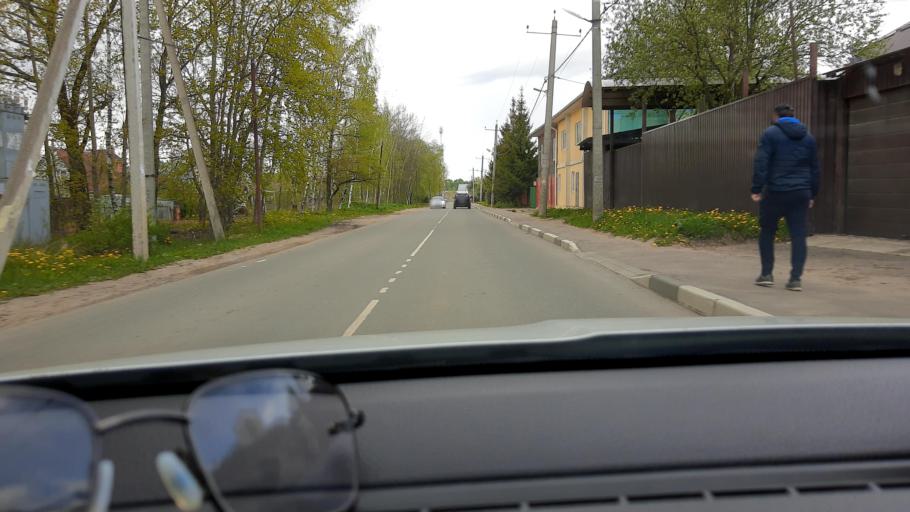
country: RU
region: Moskovskaya
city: Skhodnya
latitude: 55.8905
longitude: 37.3053
